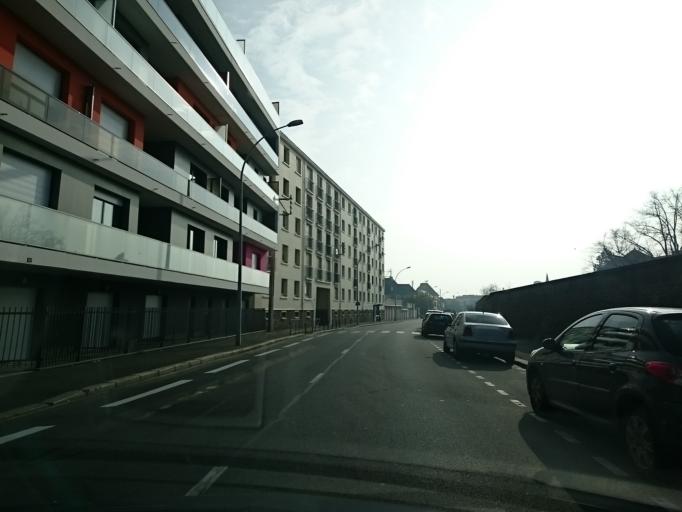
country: FR
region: Brittany
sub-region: Departement d'Ille-et-Vilaine
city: Rennes
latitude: 48.1146
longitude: -1.6510
